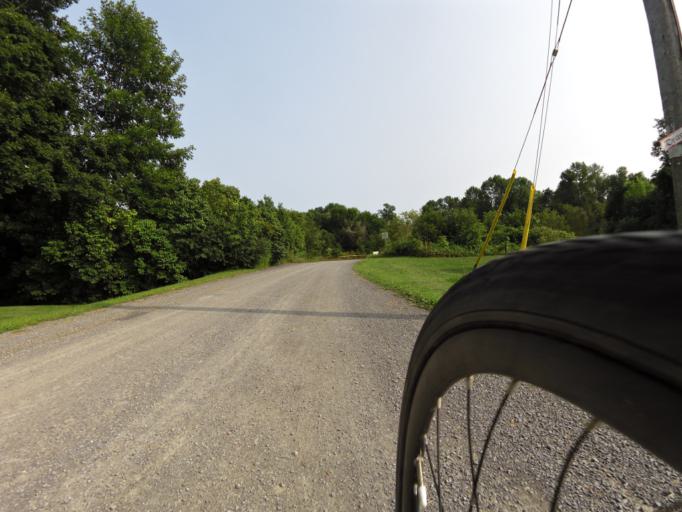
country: CA
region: Ontario
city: Quinte West
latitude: 44.0479
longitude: -77.6275
